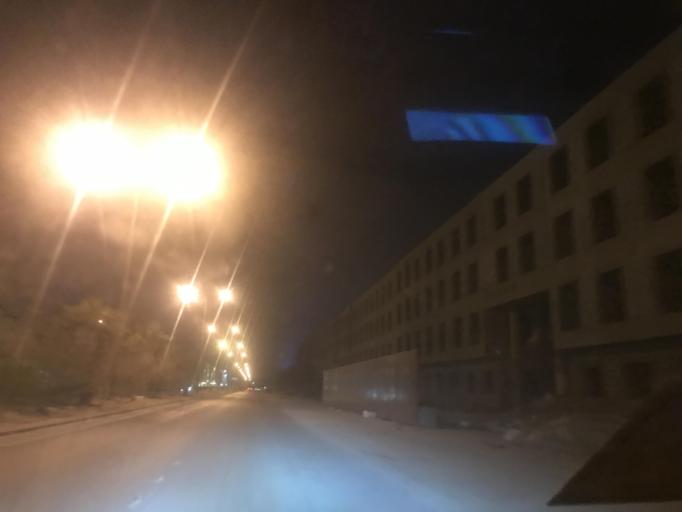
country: SA
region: Ar Riyad
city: Riyadh
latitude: 24.8045
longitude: 46.5913
